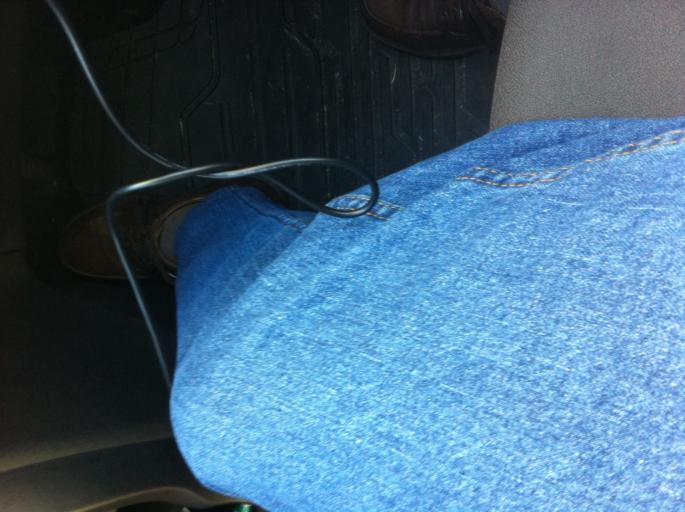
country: FR
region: Aquitaine
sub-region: Departement de la Dordogne
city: Riberac
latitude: 45.2482
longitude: 0.3378
